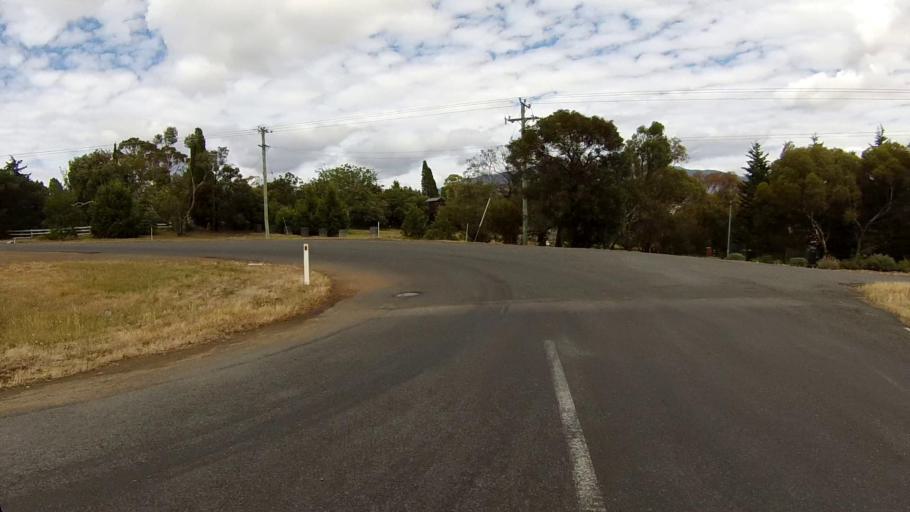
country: AU
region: Tasmania
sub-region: Brighton
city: Old Beach
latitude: -42.7970
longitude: 147.2891
